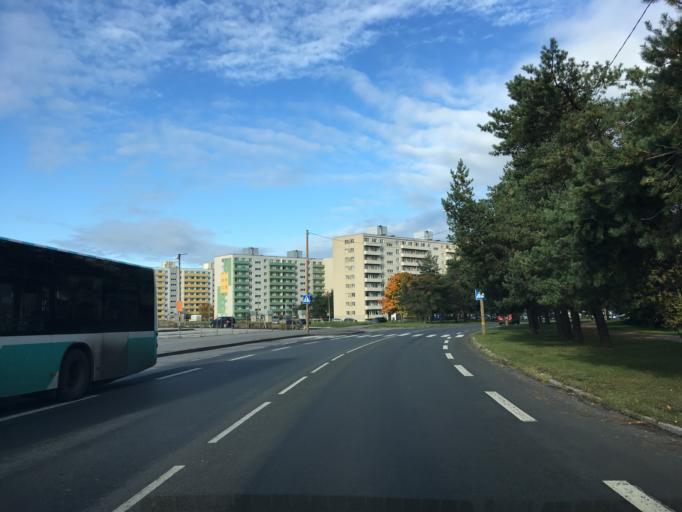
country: EE
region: Harju
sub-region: Tallinna linn
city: Tallinn
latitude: 59.3955
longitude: 24.6839
